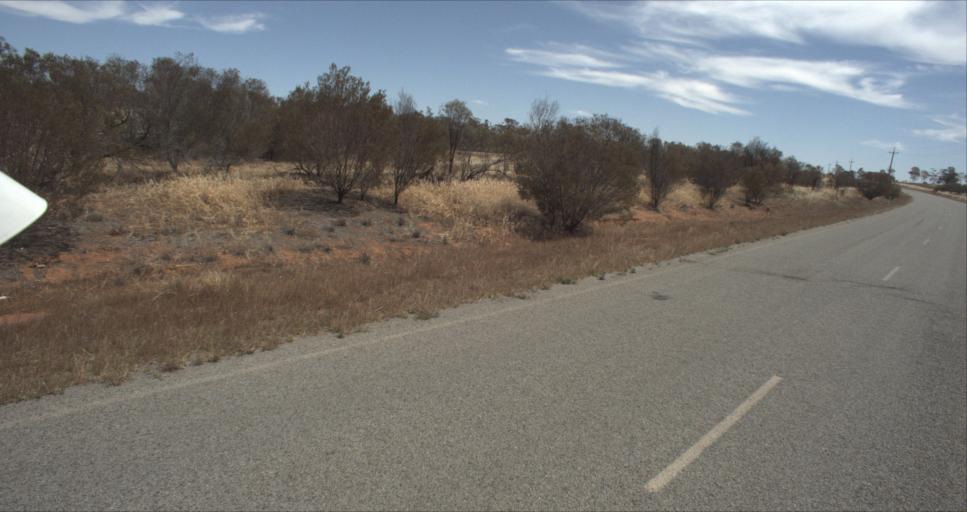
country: AU
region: New South Wales
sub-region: Leeton
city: Leeton
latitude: -34.6216
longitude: 146.4470
